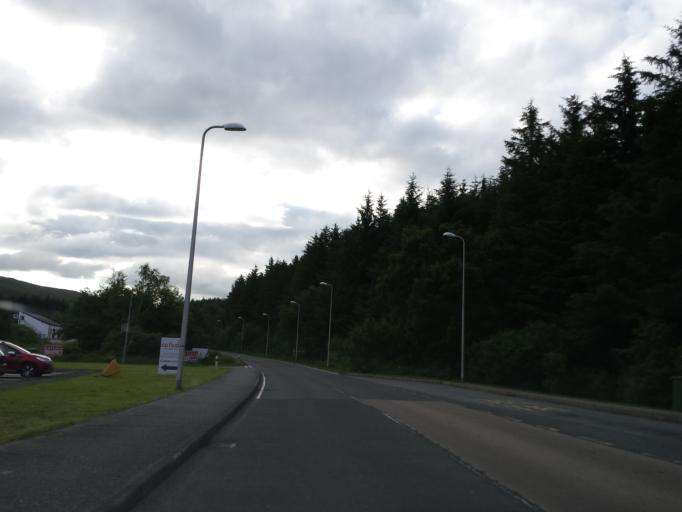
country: GB
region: Scotland
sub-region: Highland
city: Portree
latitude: 57.2431
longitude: -5.9138
